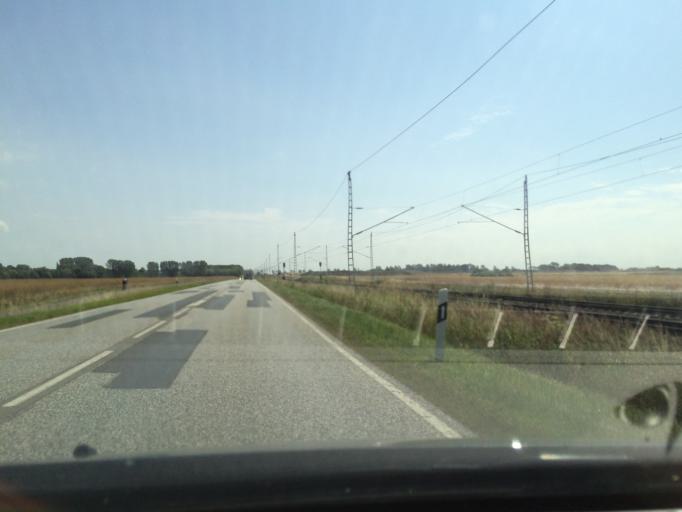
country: DE
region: Mecklenburg-Vorpommern
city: Rambin
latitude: 54.3546
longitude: 13.2242
